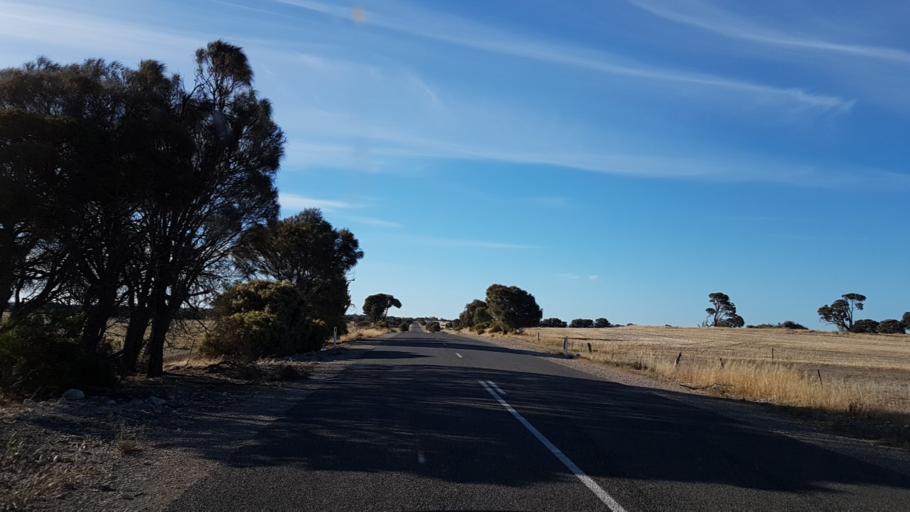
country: AU
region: South Australia
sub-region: Yorke Peninsula
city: Honiton
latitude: -34.9449
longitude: 137.0955
